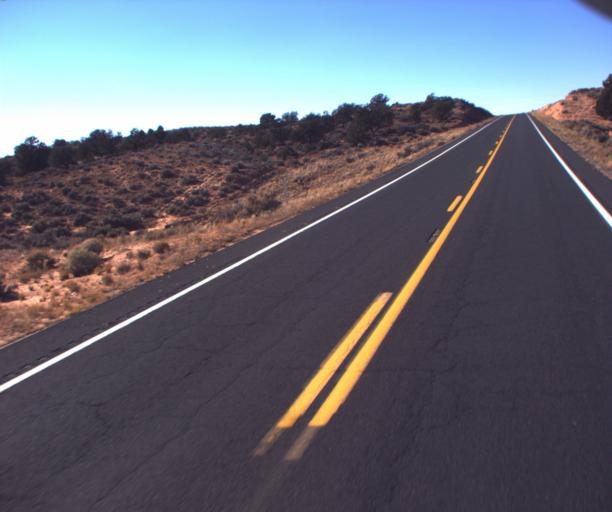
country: US
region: Arizona
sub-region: Coconino County
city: Kaibito
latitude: 36.5590
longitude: -110.7179
